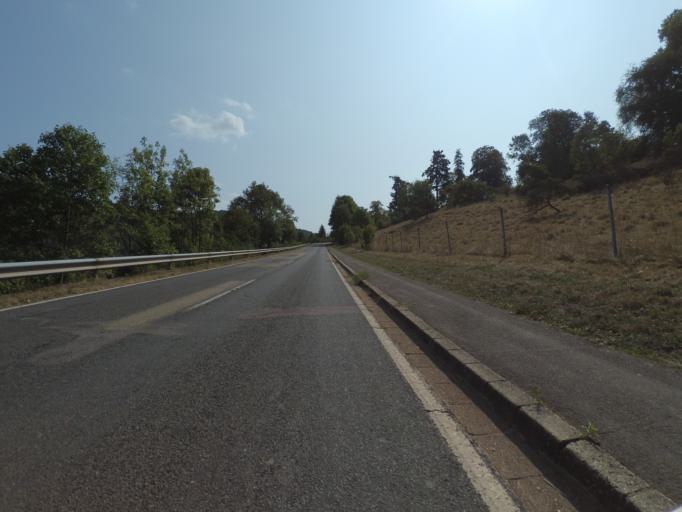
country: DE
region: Rheinland-Pfalz
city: Taben-Rodt
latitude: 49.5483
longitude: 6.6025
